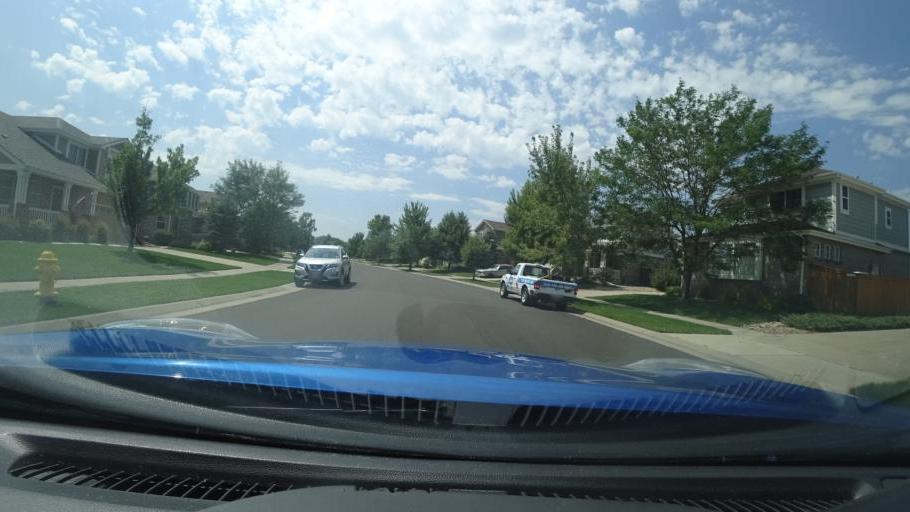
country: US
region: Colorado
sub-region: Adams County
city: Aurora
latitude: 39.6743
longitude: -104.7519
